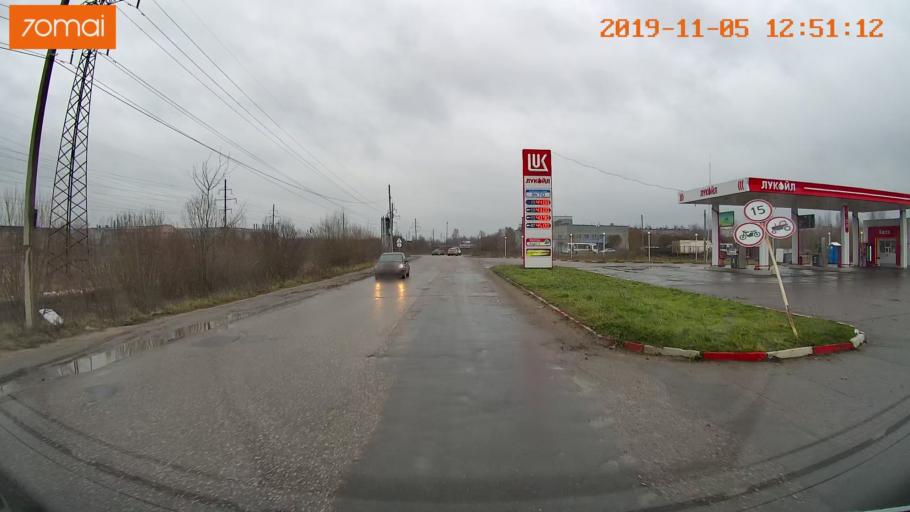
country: RU
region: Ivanovo
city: Kokhma
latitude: 56.9438
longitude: 41.1134
